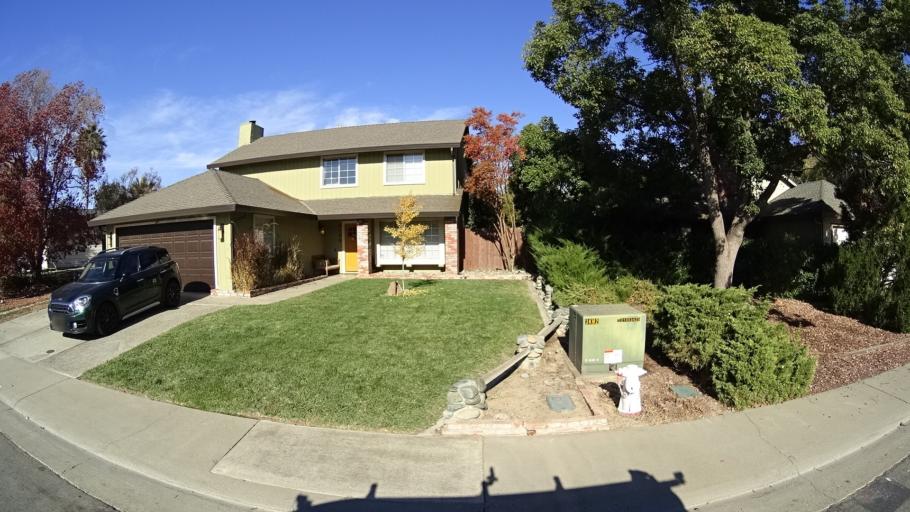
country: US
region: California
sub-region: Sacramento County
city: Antelope
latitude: 38.7114
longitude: -121.3203
